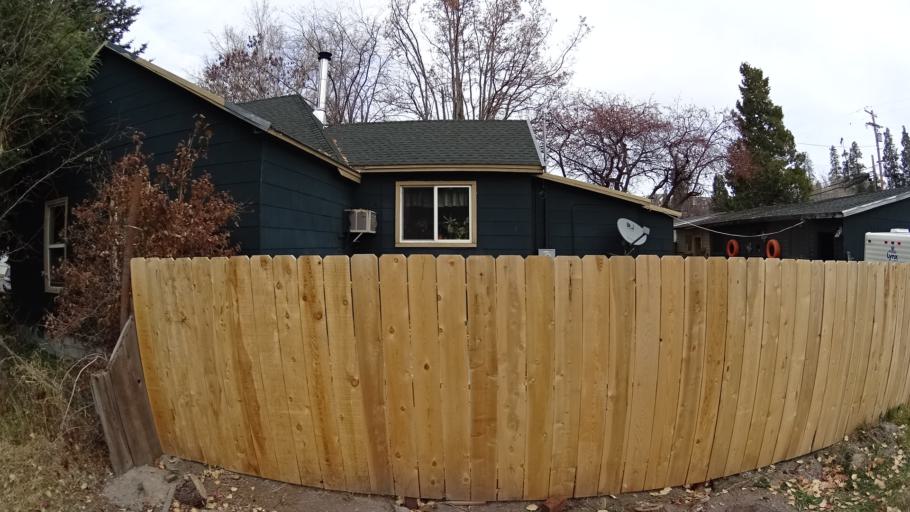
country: US
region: California
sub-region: Siskiyou County
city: Weed
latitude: 41.4270
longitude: -122.3839
